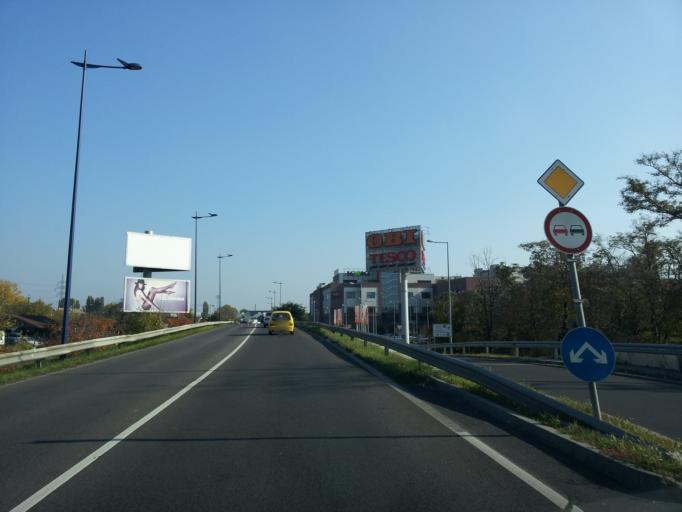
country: HU
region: Budapest
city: Budapest XIX. keruelet
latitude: 47.4641
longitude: 19.1423
